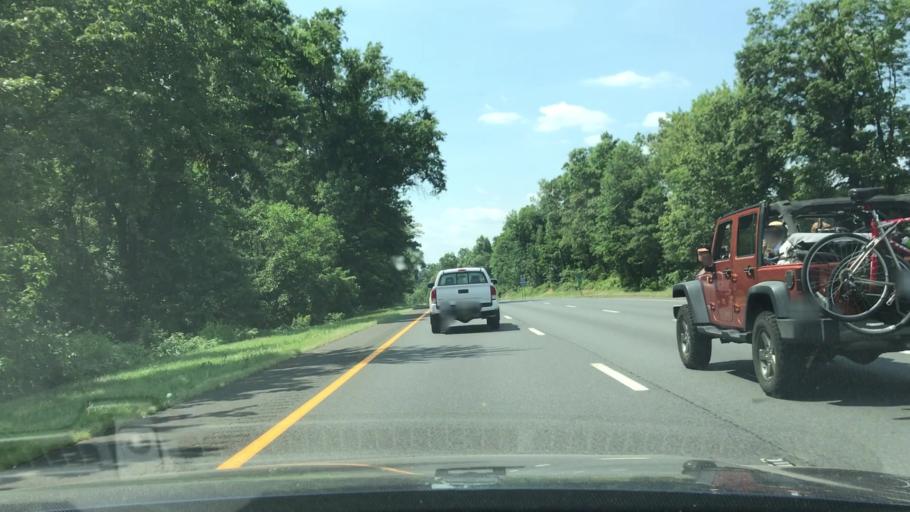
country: US
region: New Jersey
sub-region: Somerset County
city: Finderne
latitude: 40.5778
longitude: -74.5710
